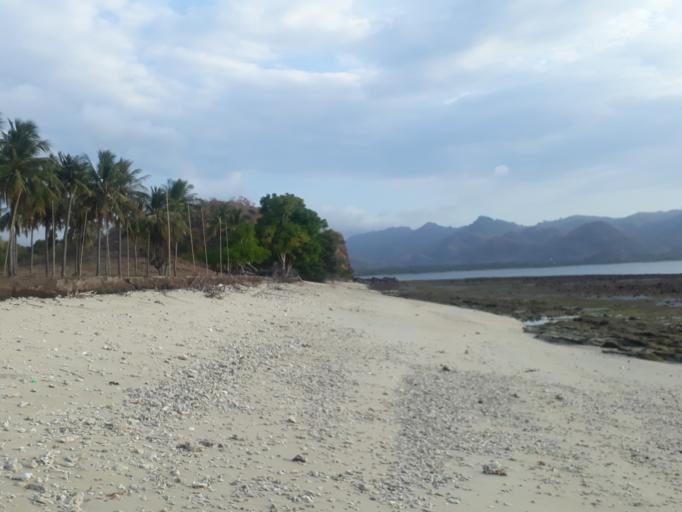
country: ID
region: West Nusa Tenggara
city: Tawun
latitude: -8.7346
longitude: 115.8827
